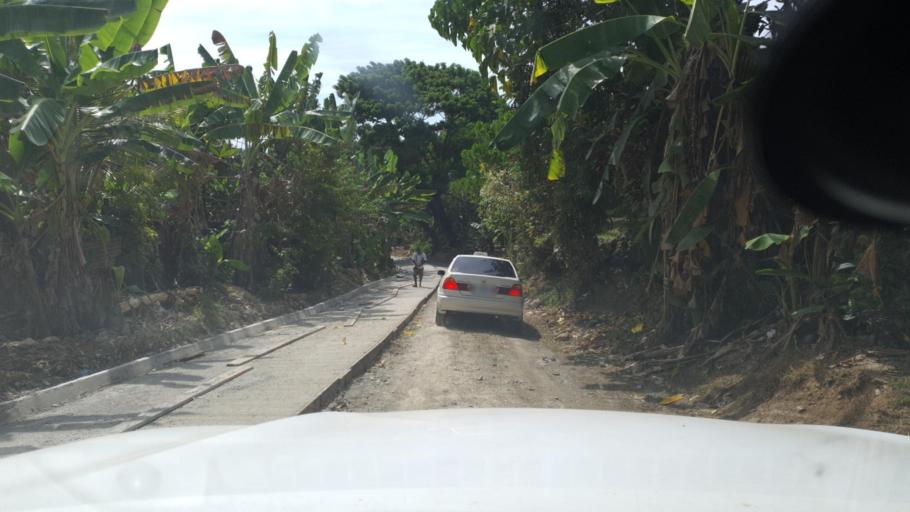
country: SB
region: Guadalcanal
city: Honiara
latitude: -9.4373
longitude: 159.9866
